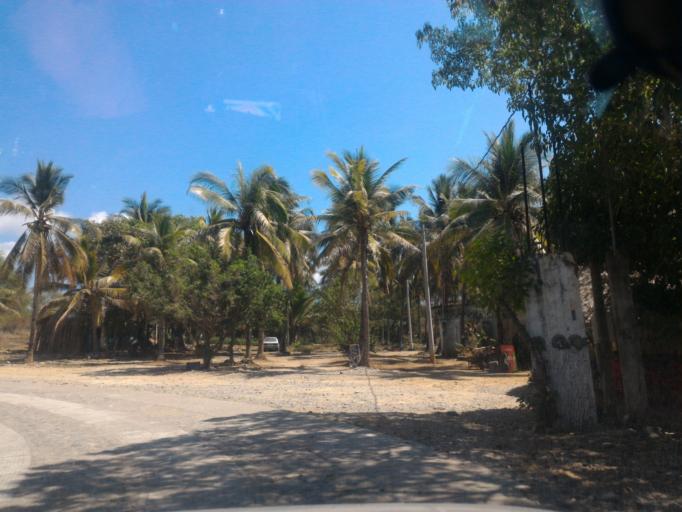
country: MX
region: Michoacan
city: Coahuayana Viejo
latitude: 18.5580
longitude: -103.6391
